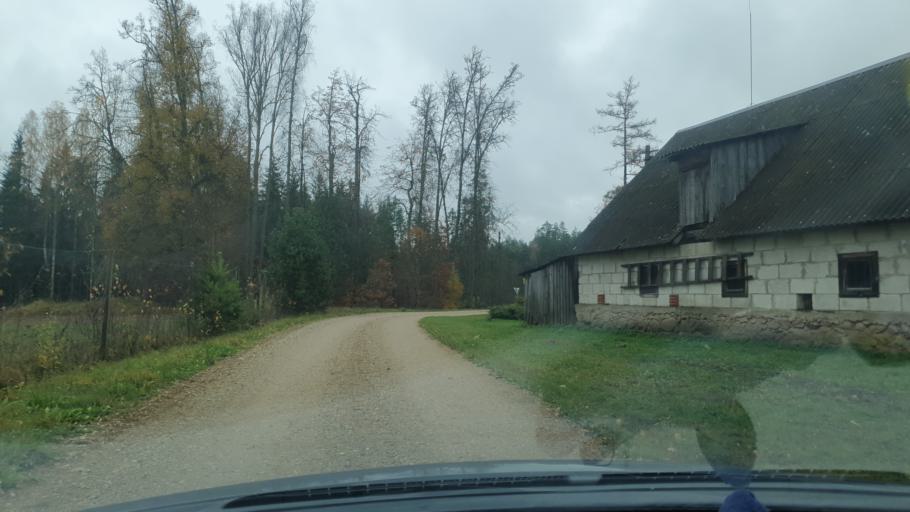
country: EE
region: Viljandimaa
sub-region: Karksi vald
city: Karksi-Nuia
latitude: 57.9917
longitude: 25.6397
